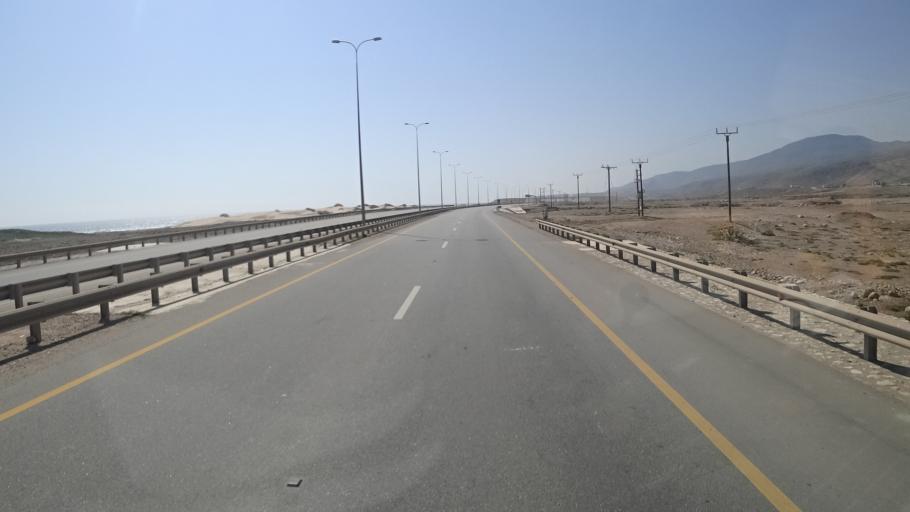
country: OM
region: Zufar
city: Salalah
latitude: 17.0262
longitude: 54.6493
